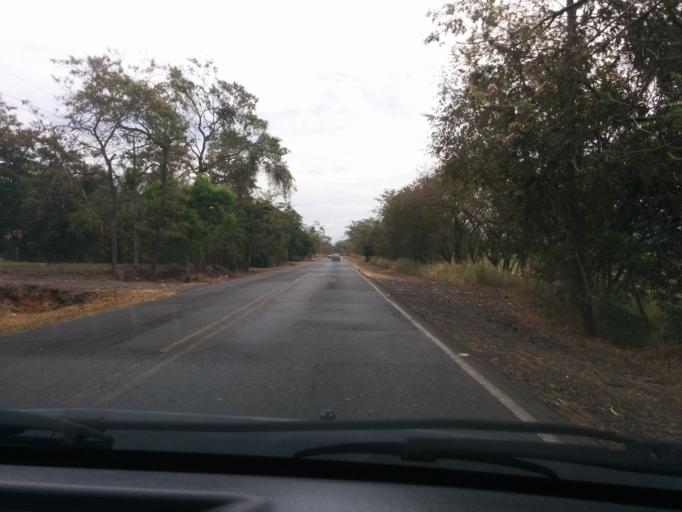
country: CR
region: Puntarenas
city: Esparza
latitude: 10.0047
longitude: -84.6278
